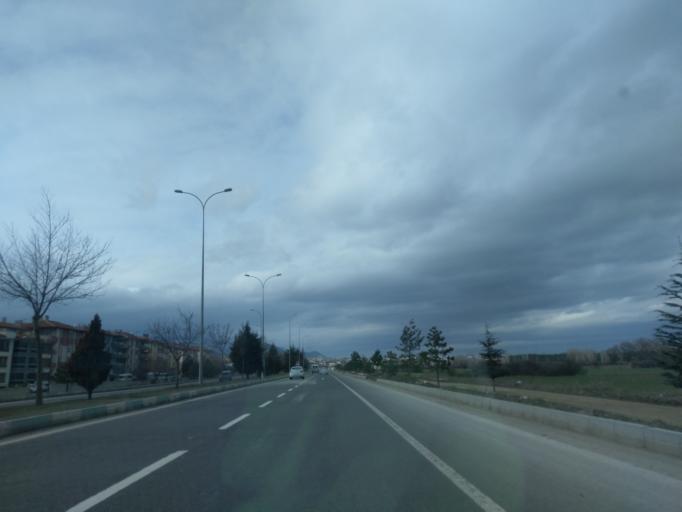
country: TR
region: Kuetahya
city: Kutahya
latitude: 39.4114
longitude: 30.0175
